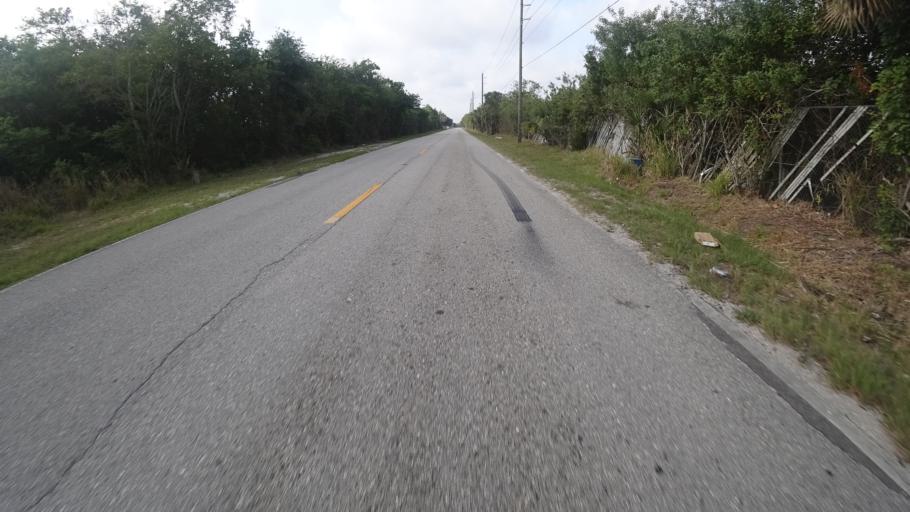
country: US
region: Florida
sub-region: Manatee County
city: Whitfield
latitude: 27.4254
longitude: -82.5219
